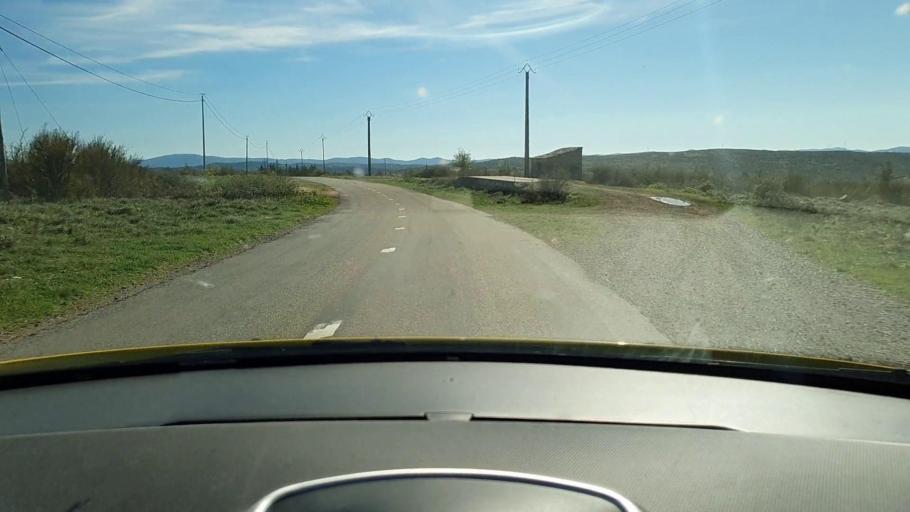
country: FR
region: Languedoc-Roussillon
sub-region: Departement du Gard
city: Aveze
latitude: 43.9559
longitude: 3.4143
